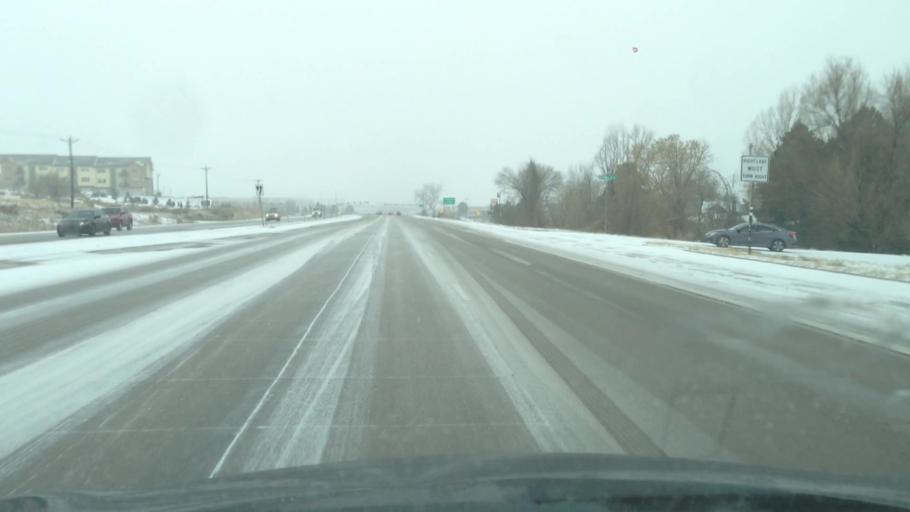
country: US
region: Colorado
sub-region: Douglas County
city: Stonegate
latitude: 39.5627
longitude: -104.7830
